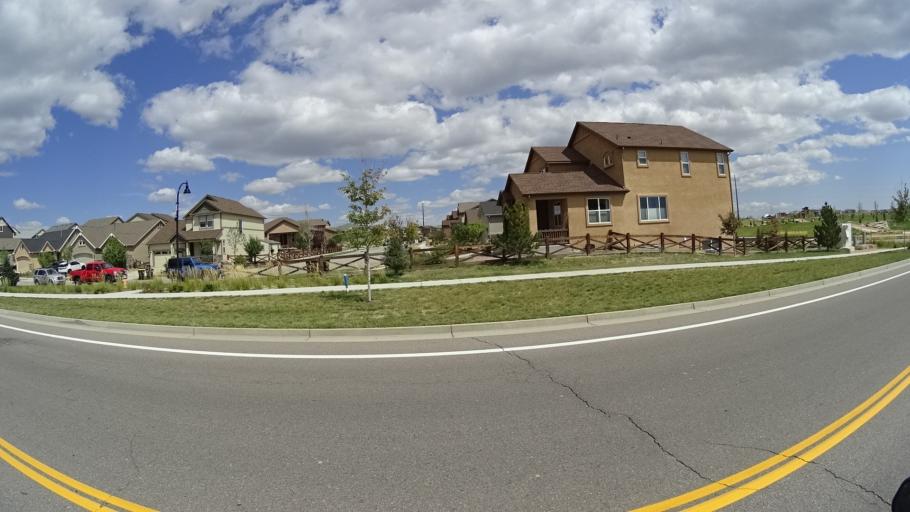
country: US
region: Colorado
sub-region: El Paso County
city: Cimarron Hills
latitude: 38.9322
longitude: -104.6677
